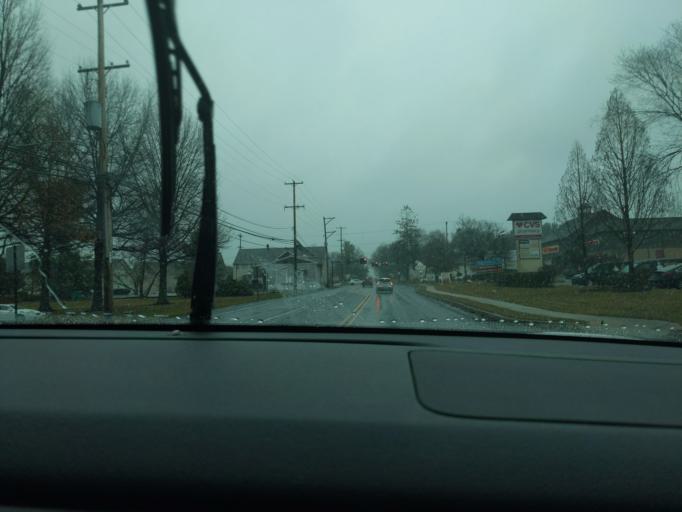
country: US
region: Pennsylvania
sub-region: Bucks County
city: Doylestown
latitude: 40.3421
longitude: -75.1525
